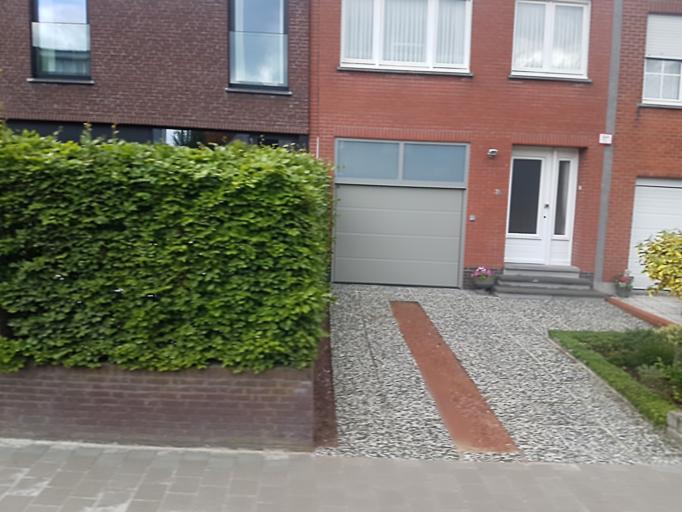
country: BE
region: Flanders
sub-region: Provincie Antwerpen
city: Kapellen
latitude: 51.2826
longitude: 4.4484
